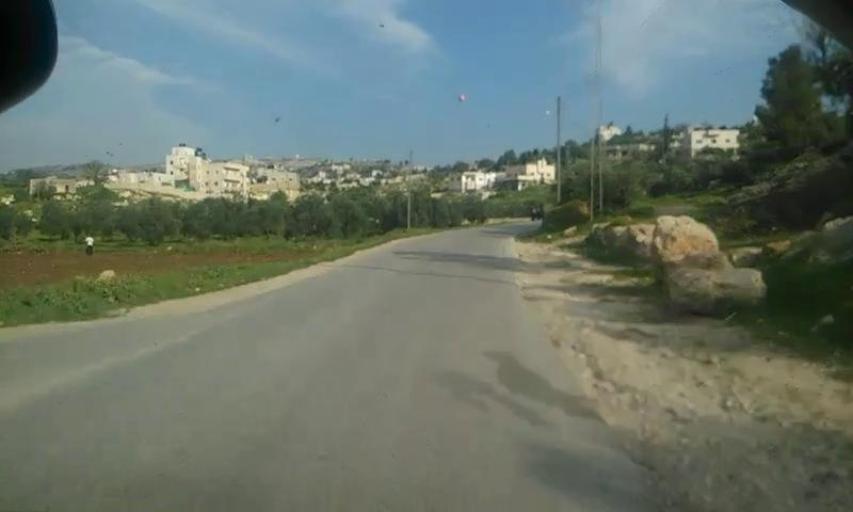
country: PS
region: West Bank
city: Nuba
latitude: 31.6134
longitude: 35.0334
